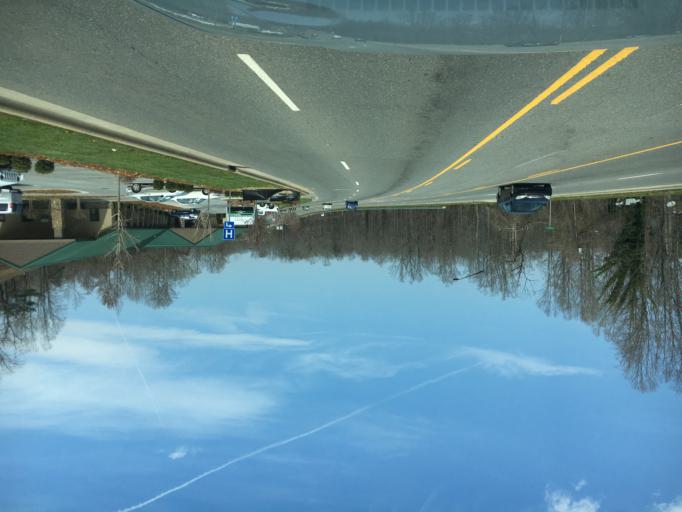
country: US
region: North Carolina
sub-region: McDowell County
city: West Marion
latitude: 35.6625
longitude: -82.0241
